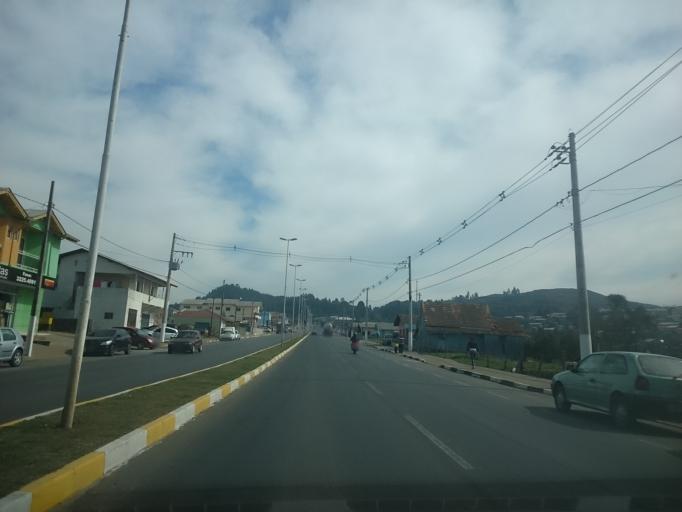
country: BR
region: Santa Catarina
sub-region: Lages
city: Lages
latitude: -27.8306
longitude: -50.3430
